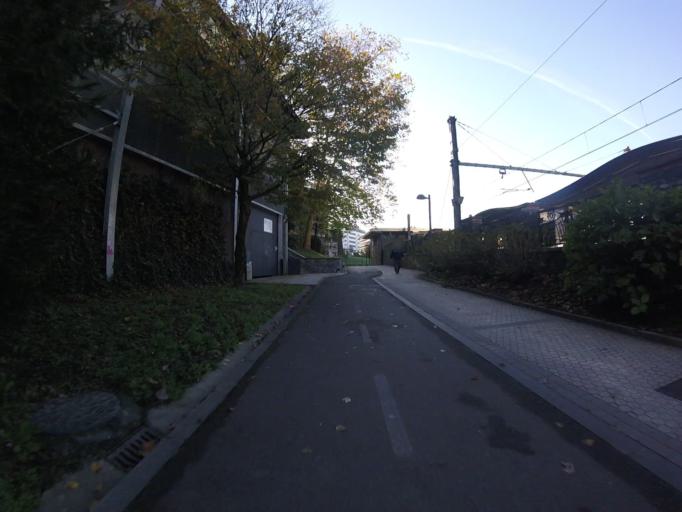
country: ES
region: Basque Country
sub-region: Provincia de Guipuzcoa
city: Lasarte
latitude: 43.2712
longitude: -2.0202
